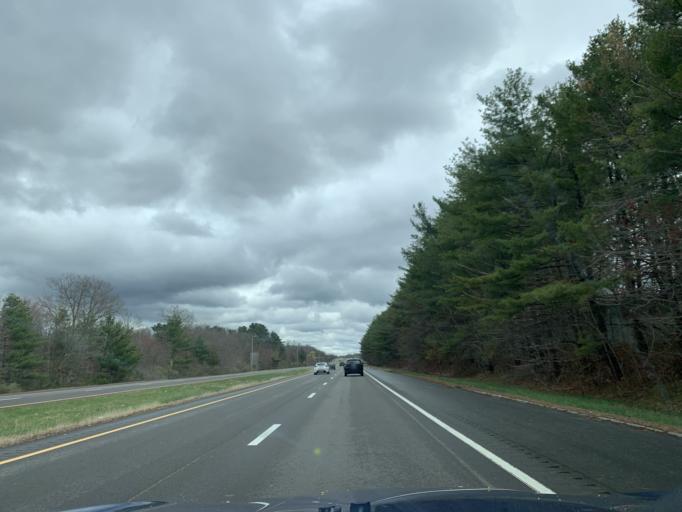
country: US
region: Massachusetts
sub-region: Bristol County
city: Mansfield
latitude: 42.0303
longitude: -71.2334
